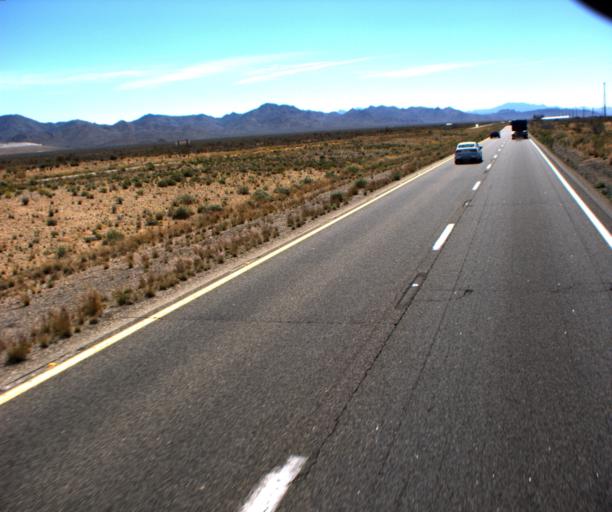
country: US
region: Arizona
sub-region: Mohave County
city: Golden Valley
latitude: 35.3456
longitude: -114.2225
